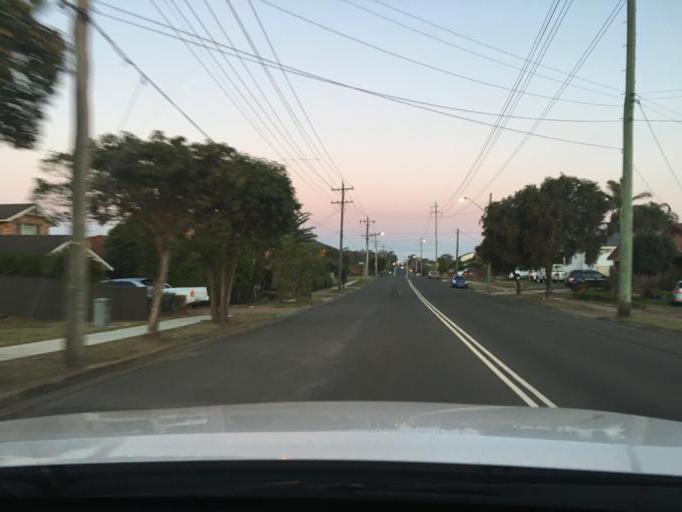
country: AU
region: New South Wales
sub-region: Holroyd
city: Girraween
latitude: -33.8274
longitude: 150.9335
